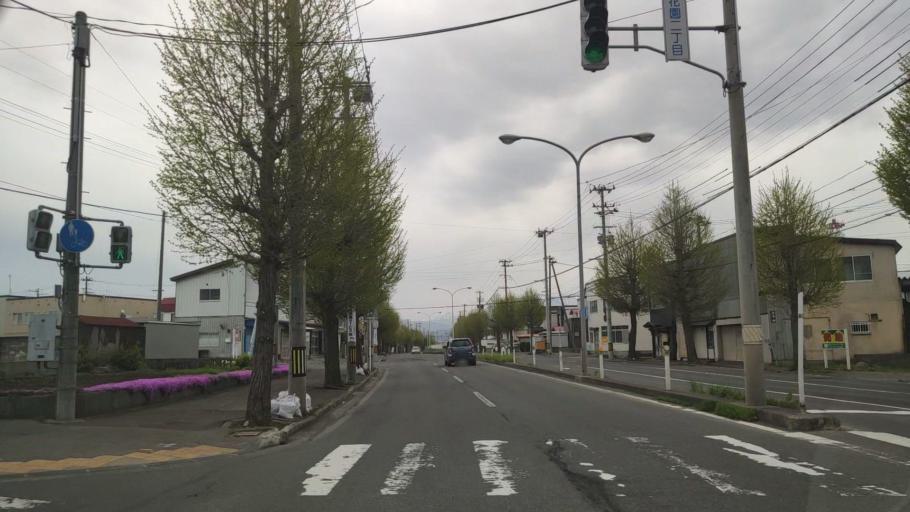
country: JP
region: Aomori
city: Aomori Shi
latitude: 40.8218
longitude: 140.7707
